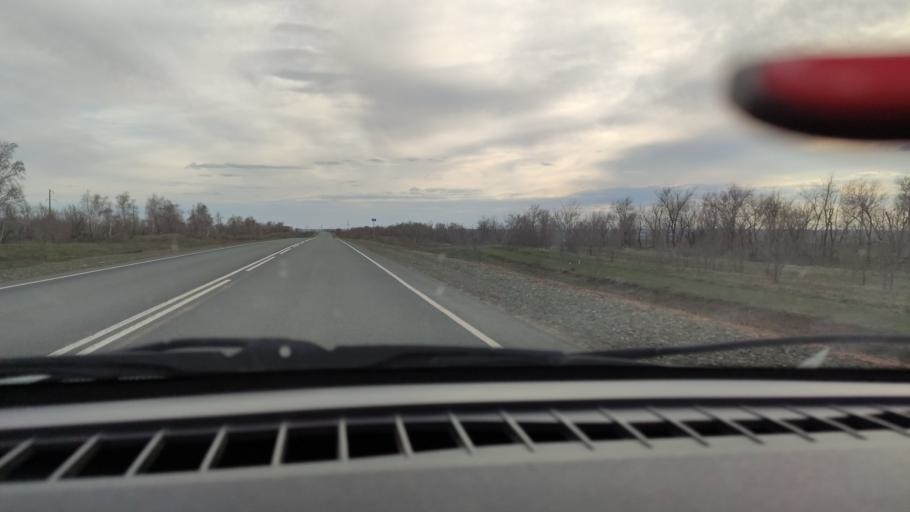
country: RU
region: Orenburg
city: Sakmara
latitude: 52.2734
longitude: 55.3890
